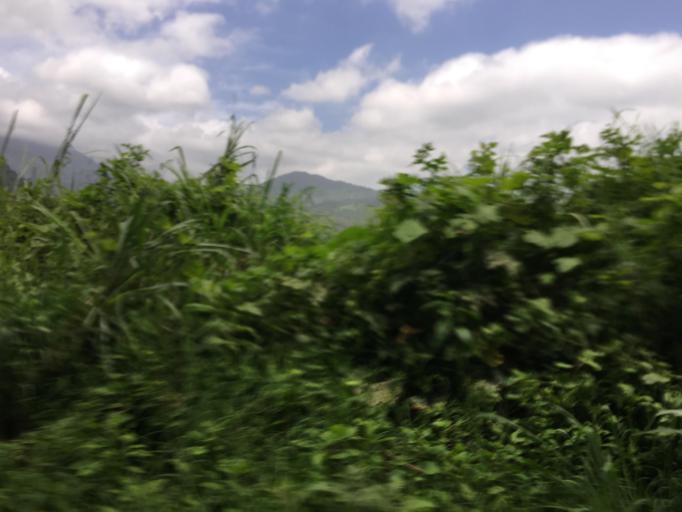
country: GT
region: Guatemala
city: Villa Canales
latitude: 14.4256
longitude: -90.5344
